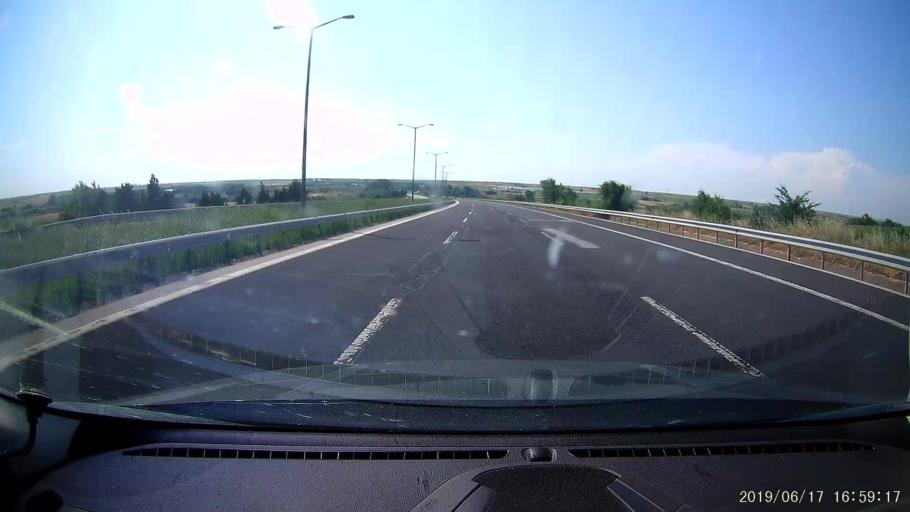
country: TR
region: Edirne
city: Haskoy
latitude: 41.6151
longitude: 26.8634
